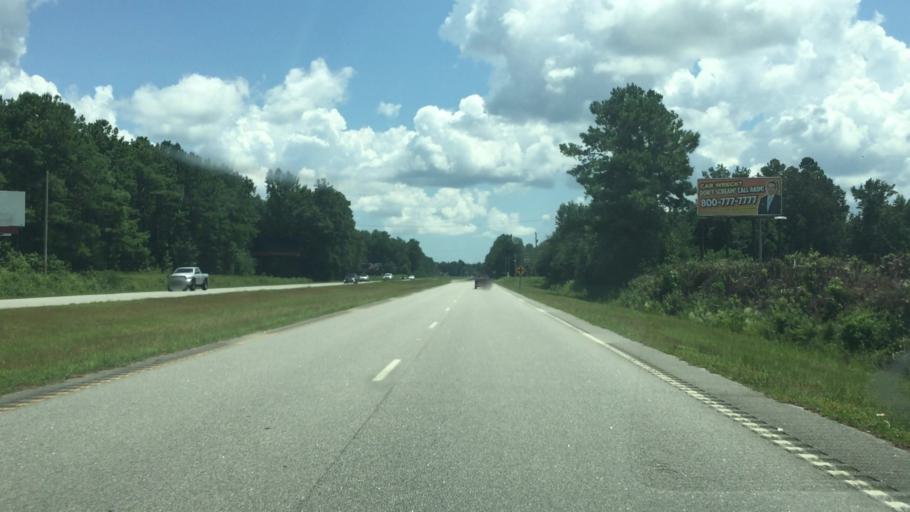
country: US
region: South Carolina
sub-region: Horry County
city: Loris
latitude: 34.0277
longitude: -78.8010
